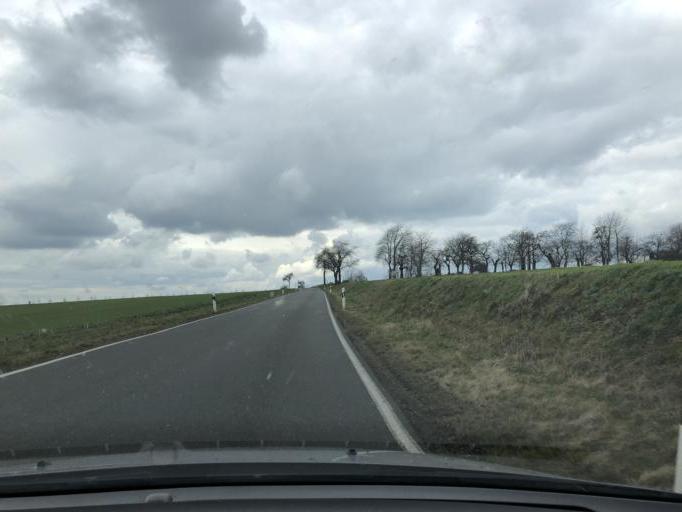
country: DE
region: Saxony
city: Grimma
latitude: 51.2461
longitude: 12.7120
